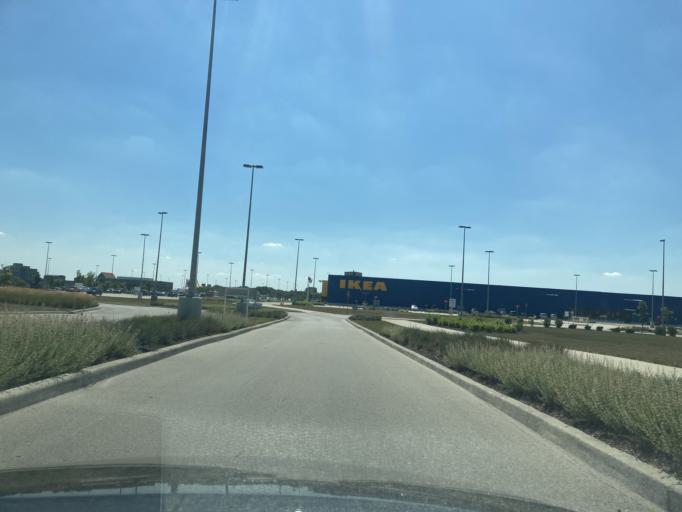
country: US
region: Indiana
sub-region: Hamilton County
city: Fishers
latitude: 39.9538
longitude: -86.0042
